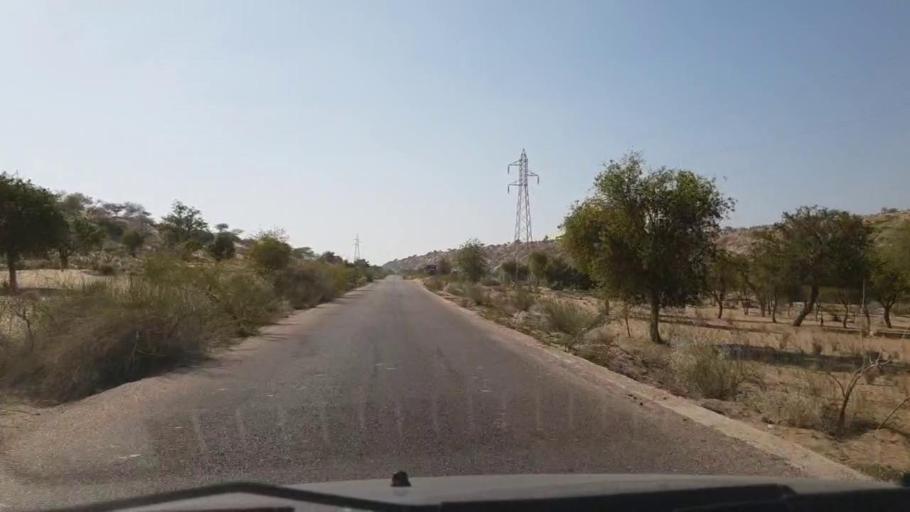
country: PK
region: Sindh
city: Diplo
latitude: 24.5575
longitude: 69.6648
